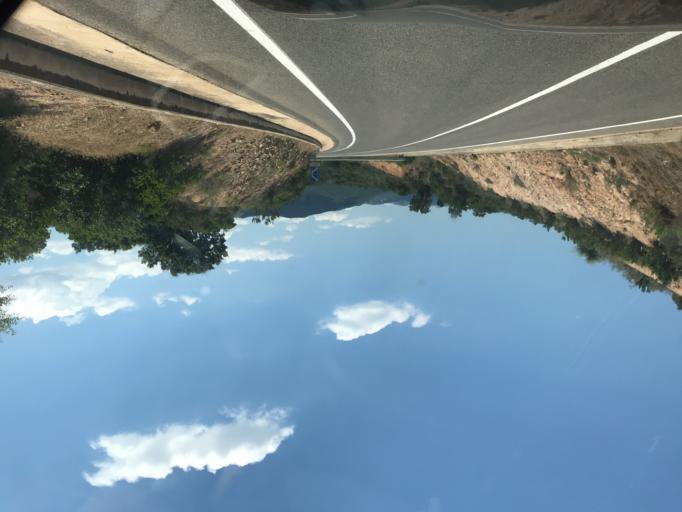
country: IT
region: Sardinia
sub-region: Provincia di Olbia-Tempio
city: Bortigiadas
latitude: 40.8572
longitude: 9.0006
